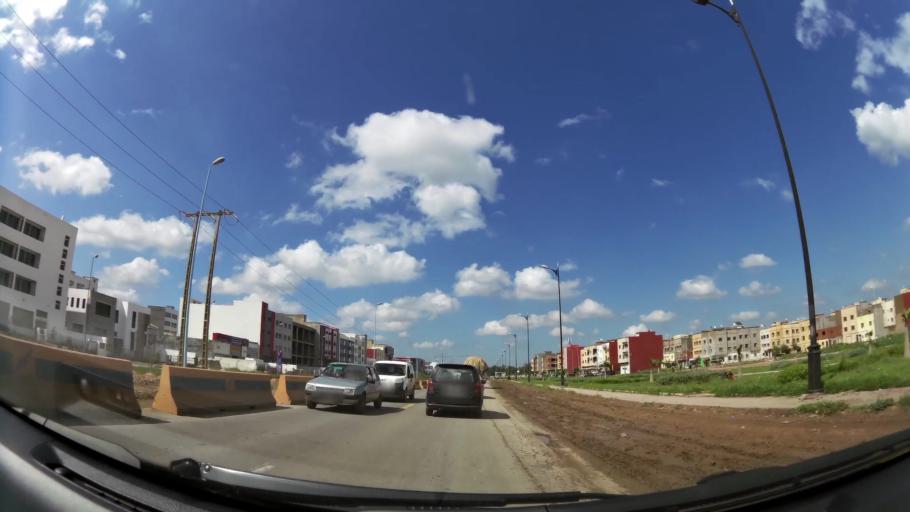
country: MA
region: Grand Casablanca
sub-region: Mediouna
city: Mediouna
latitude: 33.3990
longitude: -7.5347
